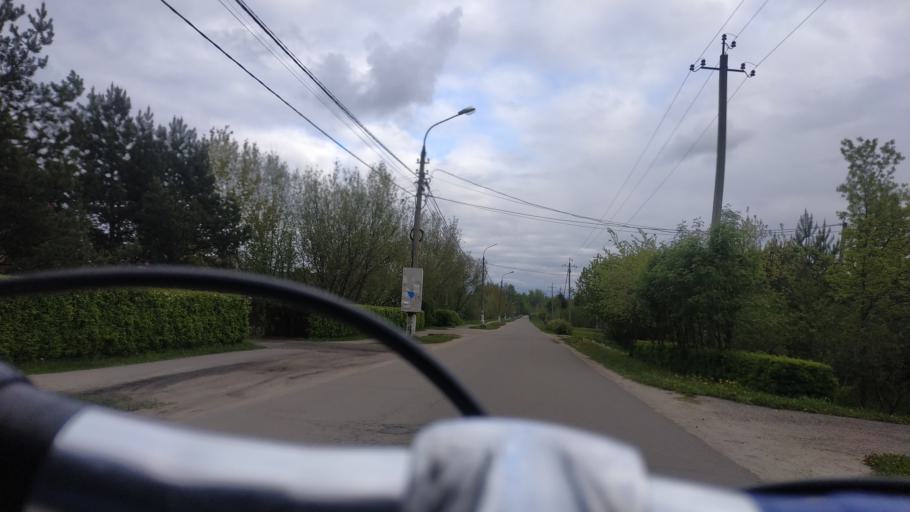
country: RU
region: Moskovskaya
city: Rechitsy
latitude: 55.6107
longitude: 38.5394
